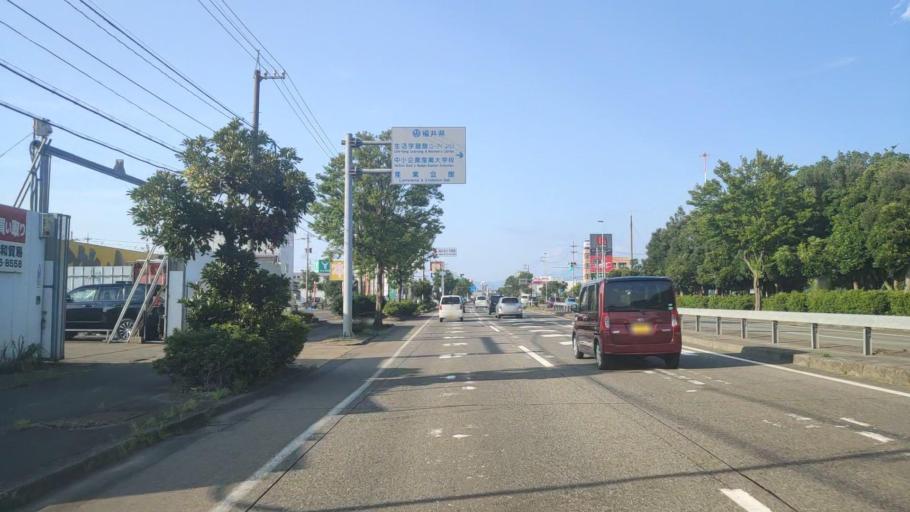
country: JP
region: Fukui
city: Fukui-shi
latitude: 36.0374
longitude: 136.2295
